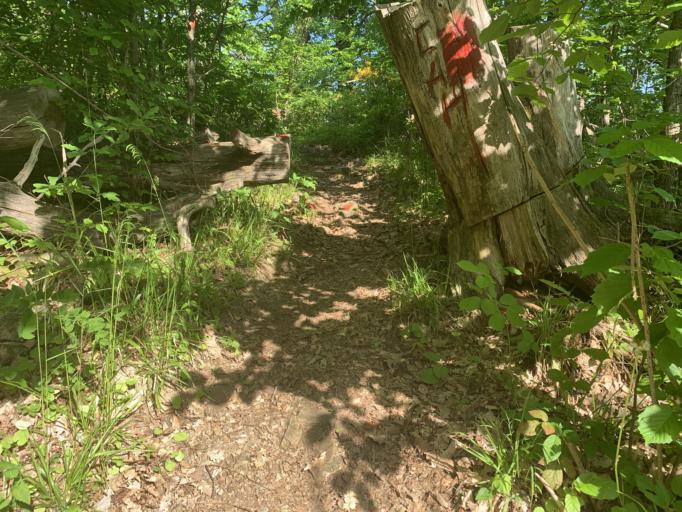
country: RU
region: Krasnodarskiy
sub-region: Sochi City
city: Lazarevskoye
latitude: 43.9511
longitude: 39.3289
